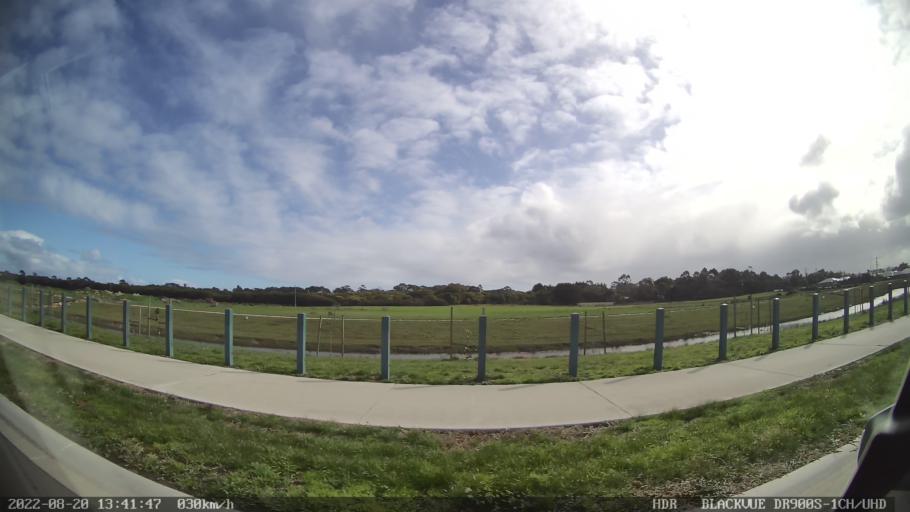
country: AU
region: Victoria
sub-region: Bass Coast
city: North Wonthaggi
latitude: -38.6006
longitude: 145.6116
